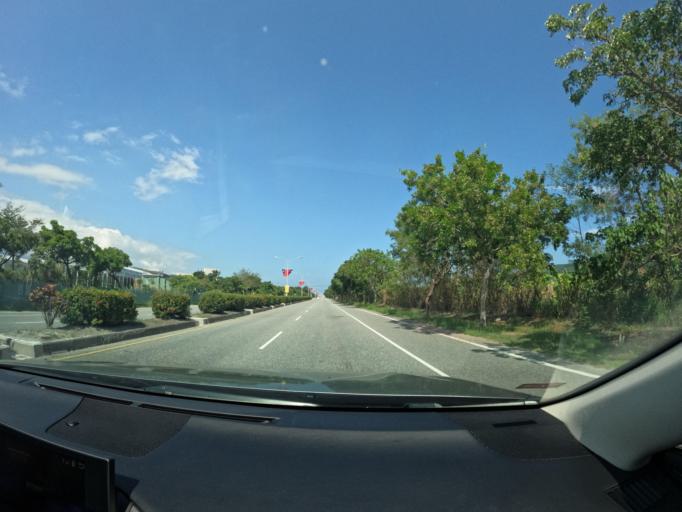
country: TW
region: Taiwan
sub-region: Hualien
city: Hualian
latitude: 23.9028
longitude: 121.5686
